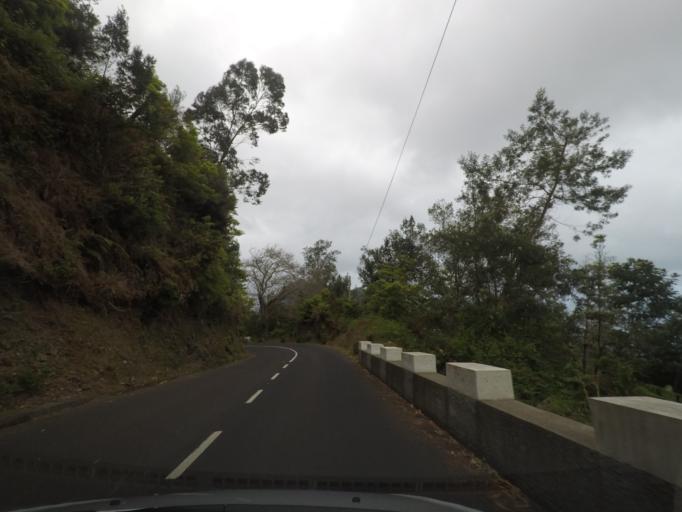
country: PT
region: Madeira
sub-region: Santana
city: Santana
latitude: 32.7496
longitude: -16.8331
